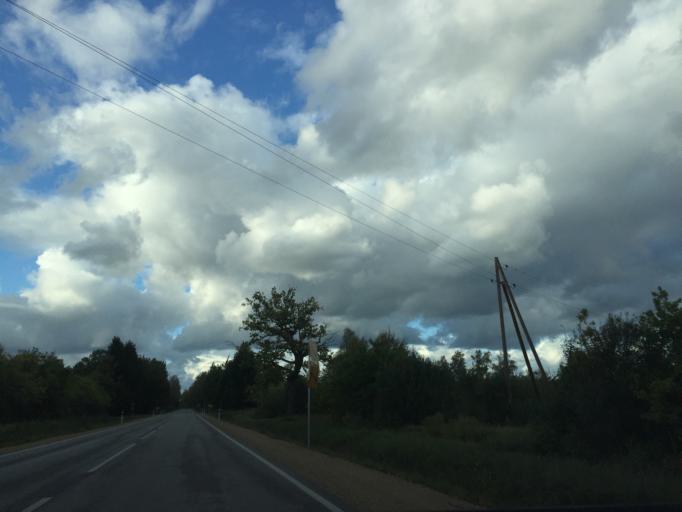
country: LV
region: Ligatne
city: Ligatne
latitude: 57.1754
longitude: 25.0408
